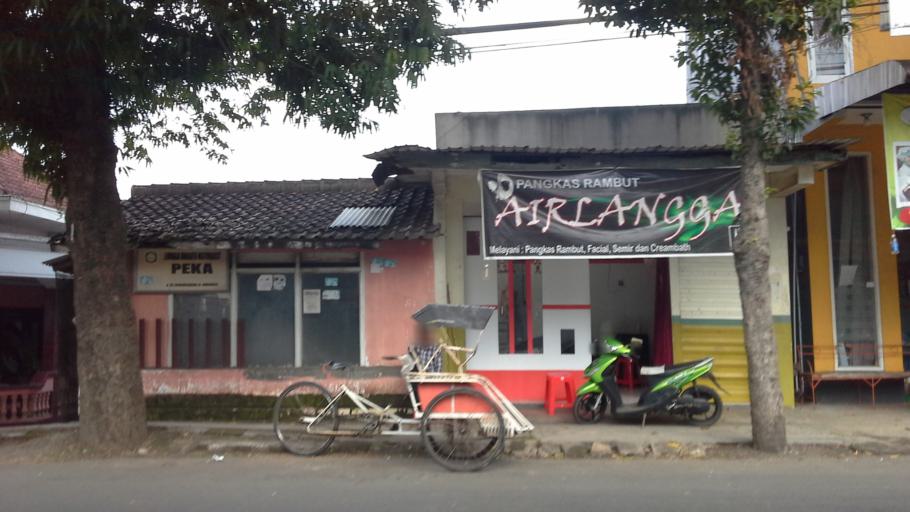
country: ID
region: East Java
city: Bondowoso
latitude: -7.9292
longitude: 113.8250
